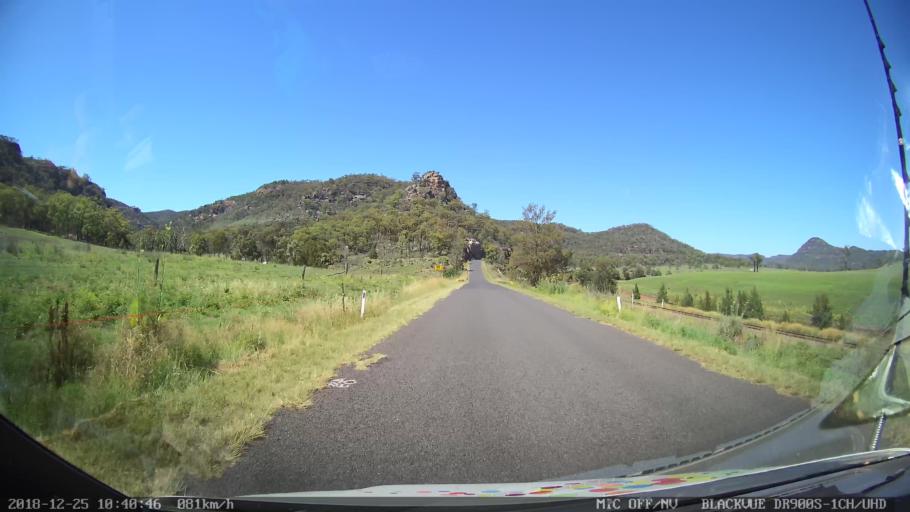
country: AU
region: New South Wales
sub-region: Upper Hunter Shire
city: Merriwa
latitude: -32.4109
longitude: 150.3409
